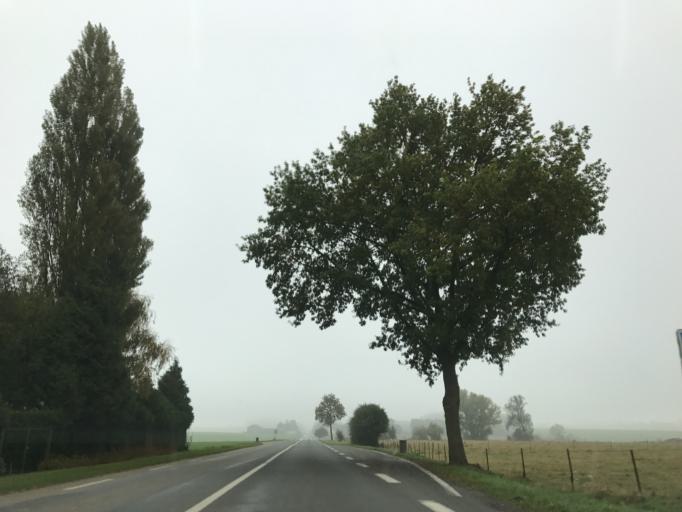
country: FR
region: Nord-Pas-de-Calais
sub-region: Departement du Pas-de-Calais
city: Bapaume
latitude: 50.0723
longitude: 2.8851
